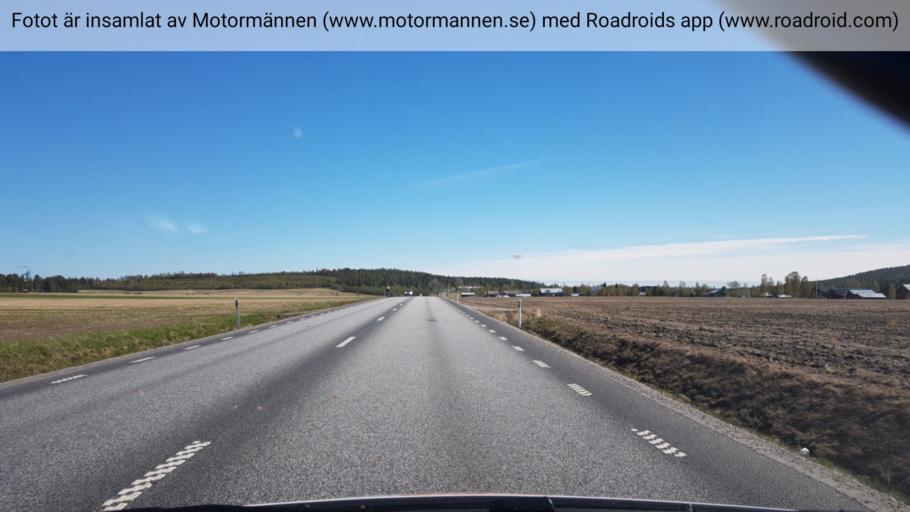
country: SE
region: Vaesterbotten
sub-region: Umea Kommun
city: Roback
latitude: 63.8718
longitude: 20.0708
